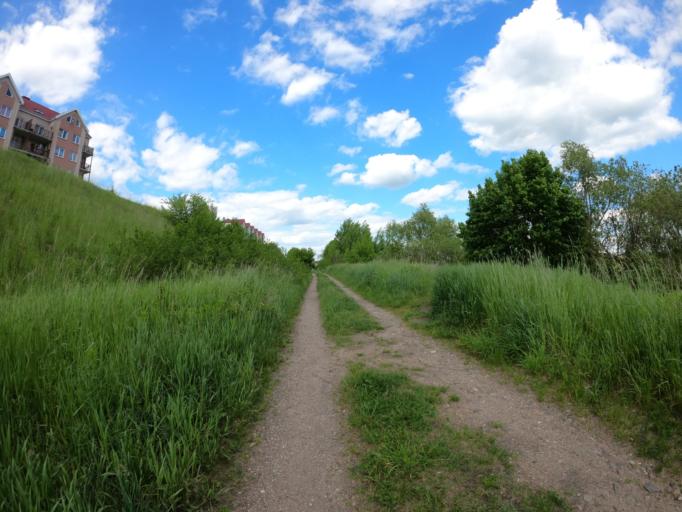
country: PL
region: Warmian-Masurian Voivodeship
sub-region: Powiat lidzbarski
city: Lidzbark Warminski
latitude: 54.1341
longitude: 20.5927
